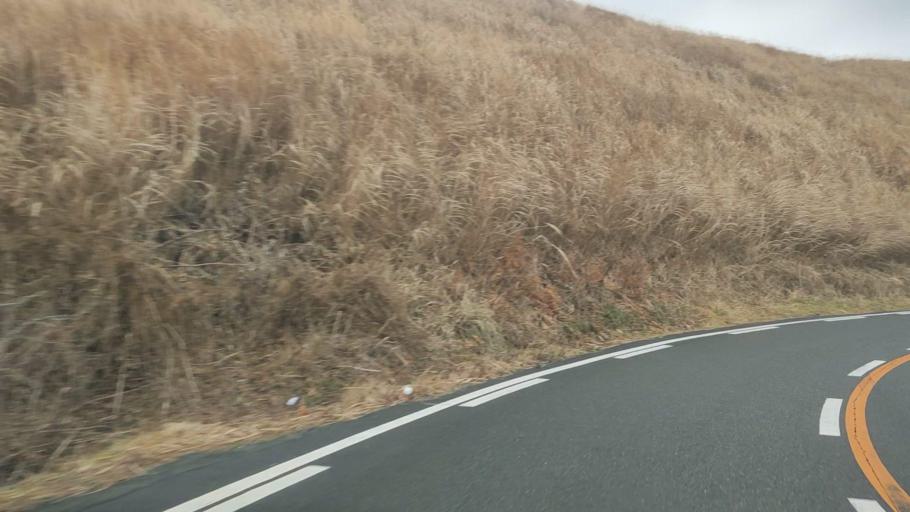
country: JP
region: Kumamoto
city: Aso
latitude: 32.9022
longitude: 131.1522
